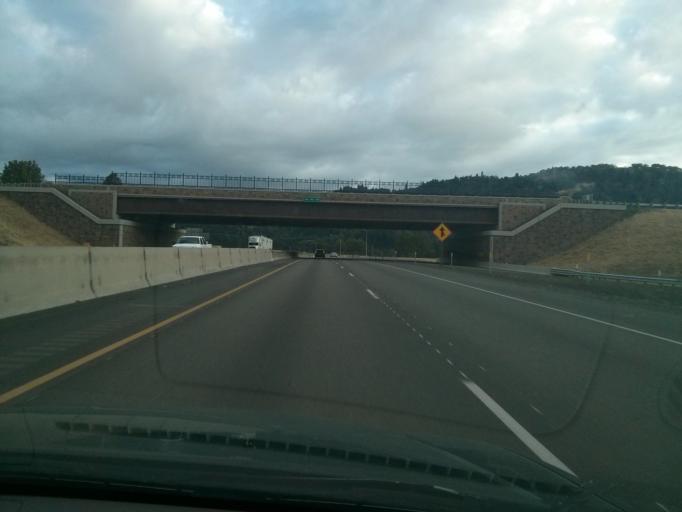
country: US
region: Oregon
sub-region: Douglas County
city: Roseburg North
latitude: 43.2908
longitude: -123.3543
